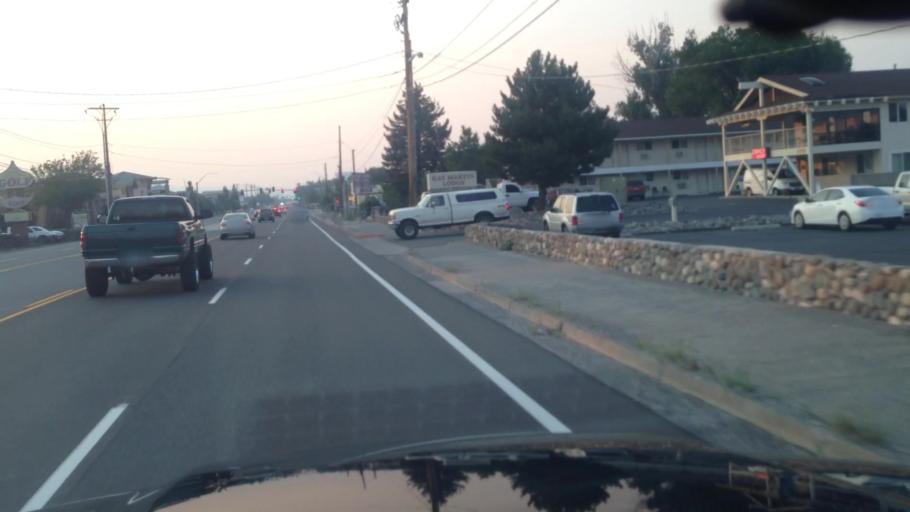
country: US
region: Nevada
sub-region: Washoe County
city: Reno
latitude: 39.4630
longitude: -119.7822
